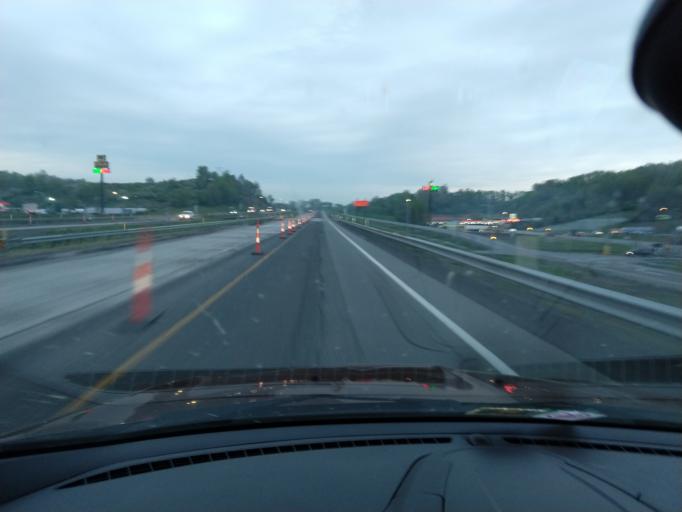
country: US
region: West Virginia
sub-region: Braxton County
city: Sutton
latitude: 38.7022
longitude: -80.6637
